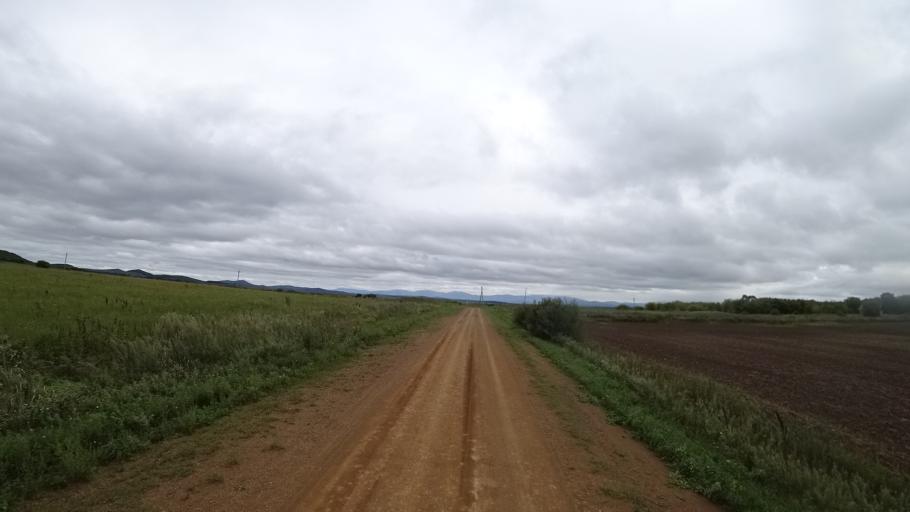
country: RU
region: Primorskiy
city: Chernigovka
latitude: 44.4353
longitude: 132.5905
